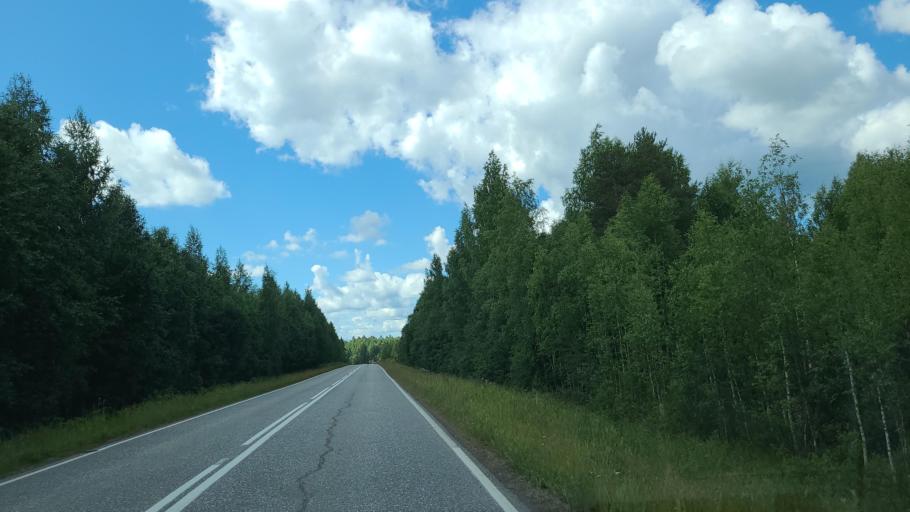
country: FI
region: Northern Savo
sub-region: Koillis-Savo
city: Kaavi
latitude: 62.9772
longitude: 28.7896
